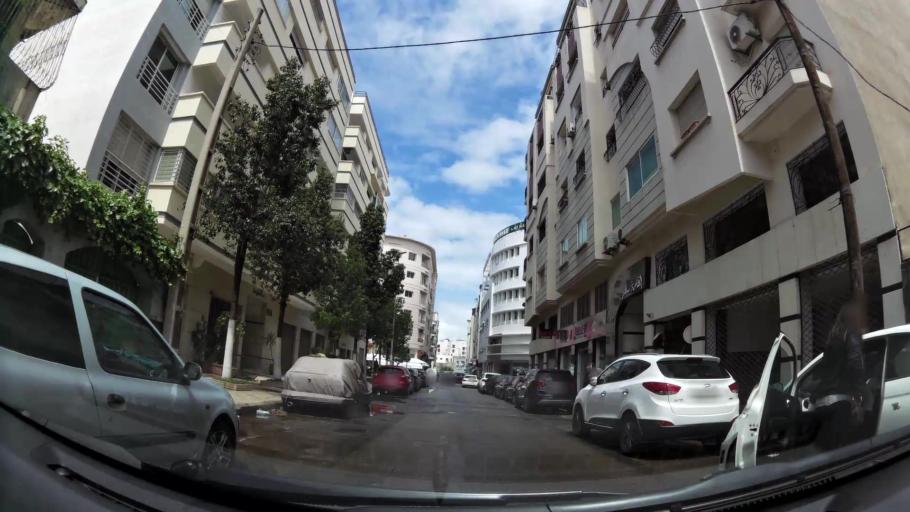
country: MA
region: Grand Casablanca
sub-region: Casablanca
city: Casablanca
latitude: 33.5753
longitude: -7.6352
